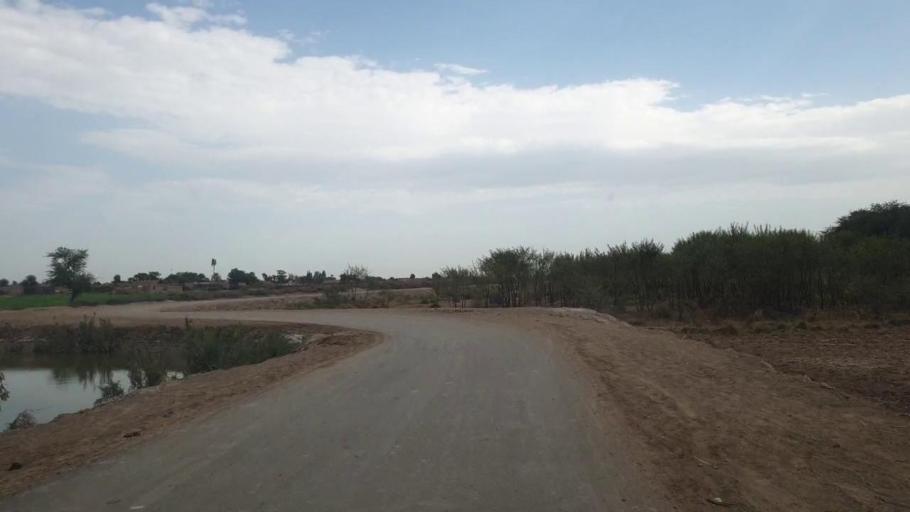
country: PK
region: Sindh
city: Hala
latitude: 25.9799
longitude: 68.4104
